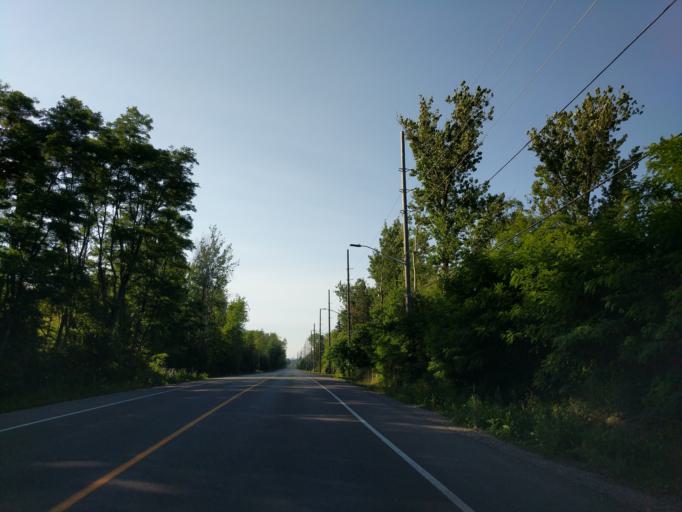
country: CA
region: Ontario
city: Oshawa
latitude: 43.9366
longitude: -78.9127
